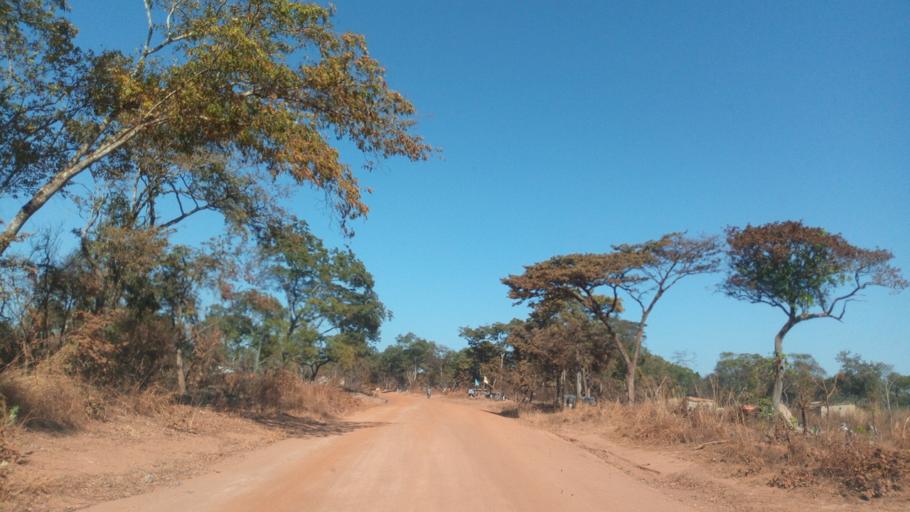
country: ZM
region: Luapula
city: Mwense
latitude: -10.7069
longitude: 28.3694
